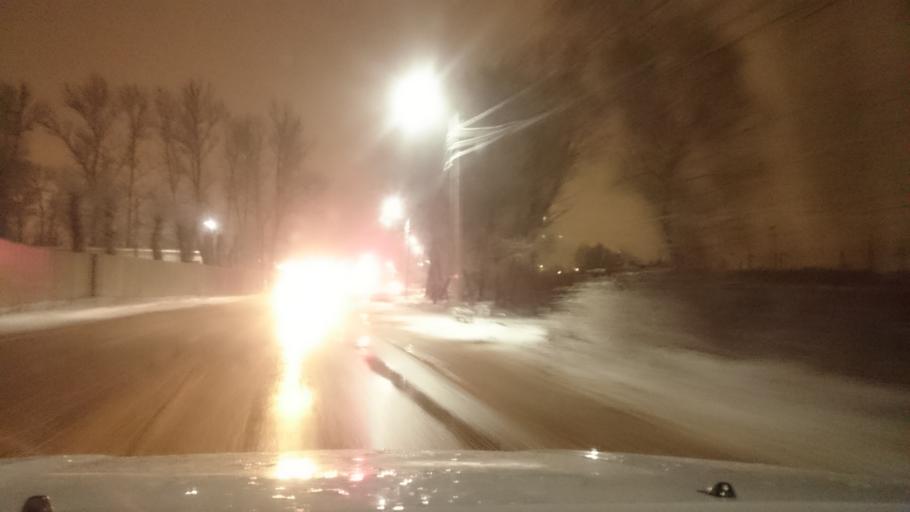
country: RU
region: Tula
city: Tula
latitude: 54.2202
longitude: 37.5917
